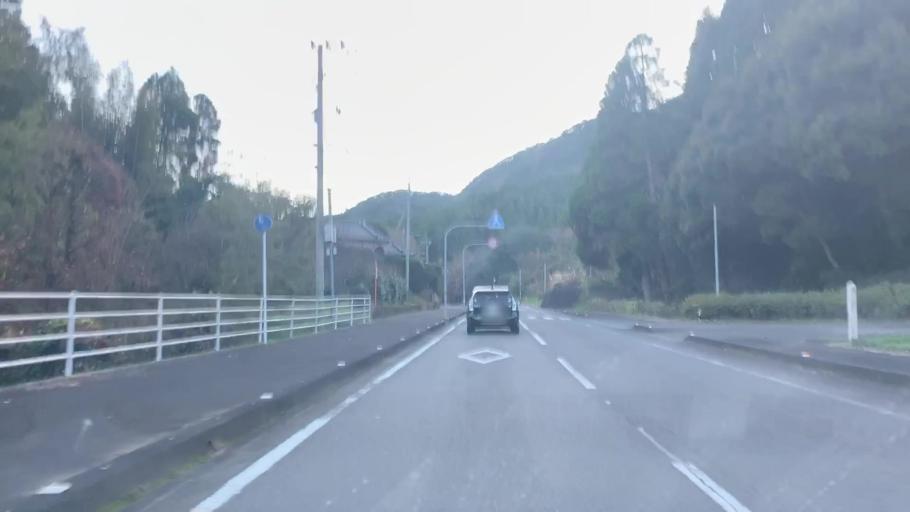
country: JP
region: Saga Prefecture
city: Imaricho-ko
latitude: 33.3219
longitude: 129.9697
